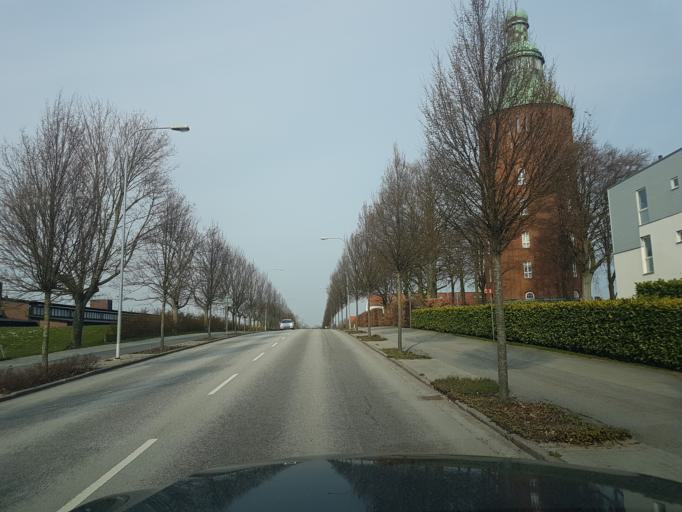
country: SE
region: Skane
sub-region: Ystads Kommun
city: Ystad
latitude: 55.4382
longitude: 13.8264
